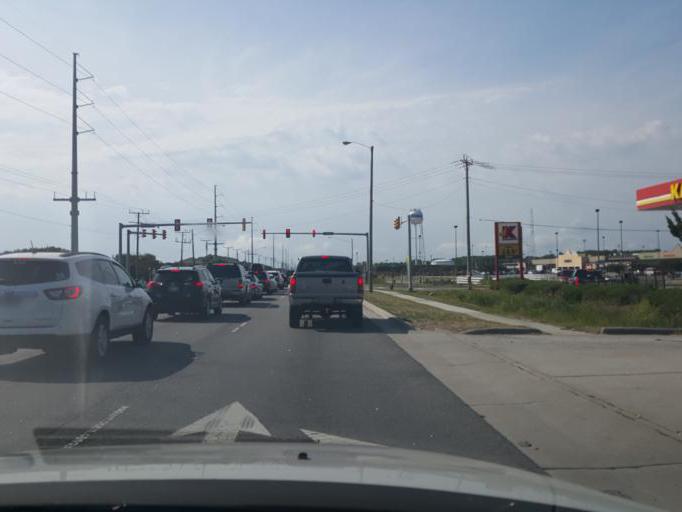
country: US
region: North Carolina
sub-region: Dare County
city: Kill Devil Hills
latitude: 36.0345
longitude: -75.6735
